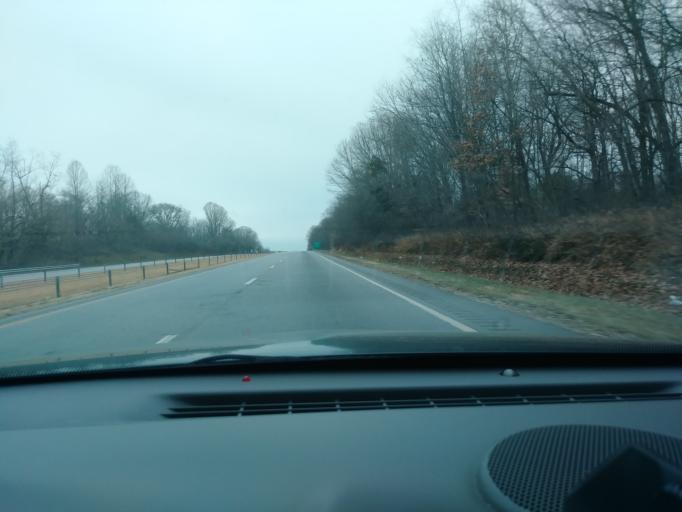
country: US
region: North Carolina
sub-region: Wilkes County
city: North Wilkesboro
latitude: 36.1379
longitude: -81.0938
